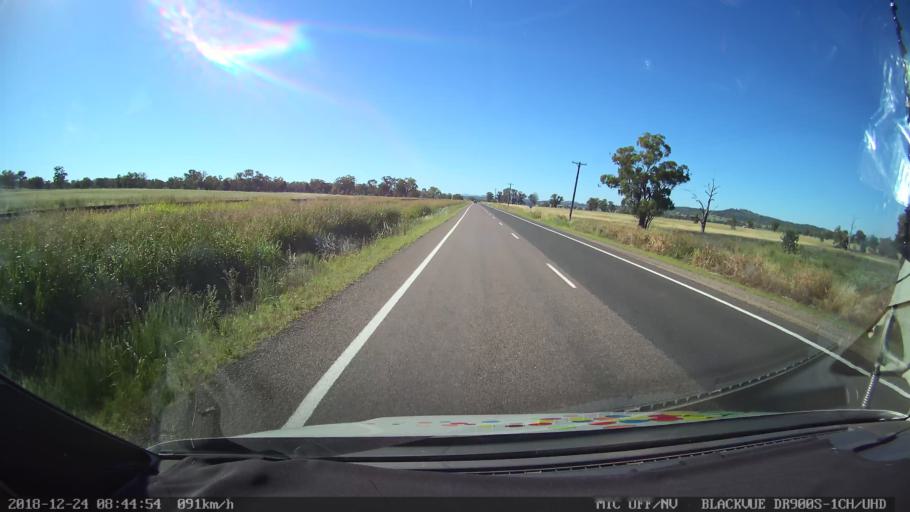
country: AU
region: New South Wales
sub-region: Liverpool Plains
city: Quirindi
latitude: -31.4080
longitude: 150.6501
